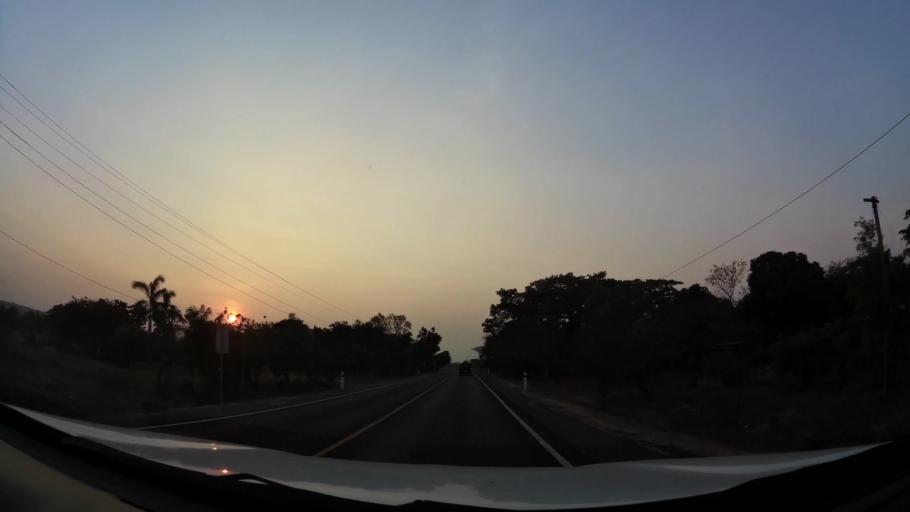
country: NI
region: Leon
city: Leon
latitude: 12.3494
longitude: -86.8264
